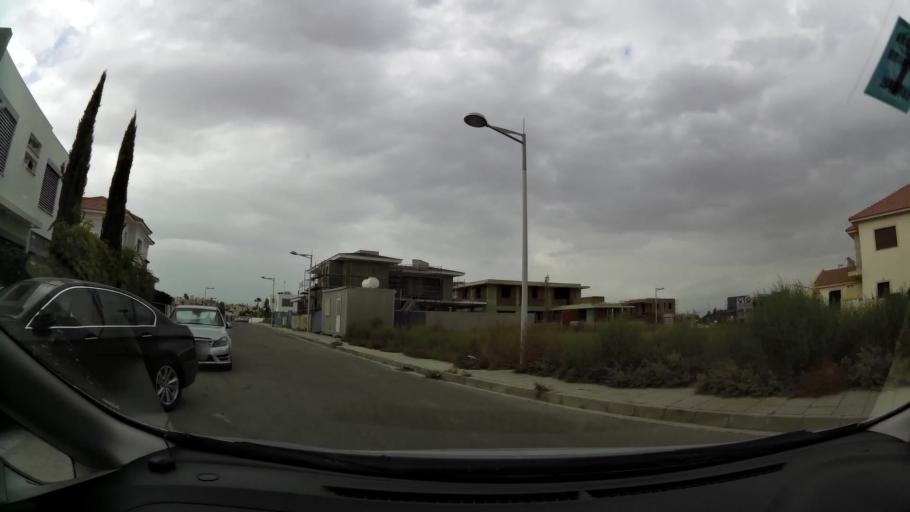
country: CY
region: Lefkosia
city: Geri
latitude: 35.1091
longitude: 33.3917
